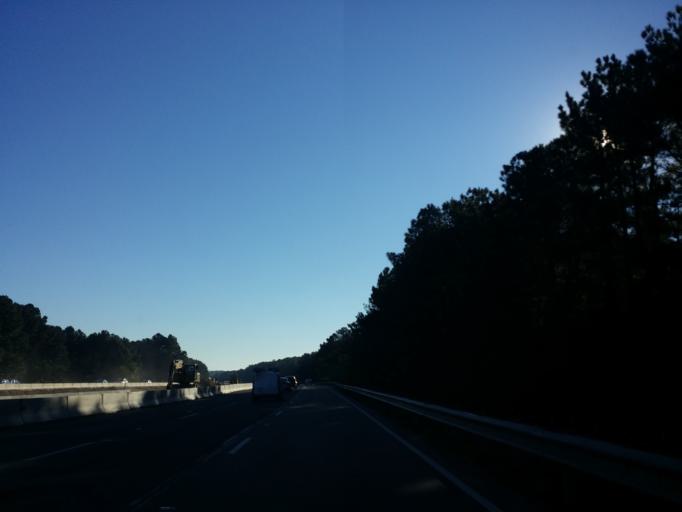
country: US
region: North Carolina
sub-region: Wake County
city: West Raleigh
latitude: 35.7515
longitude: -78.7037
